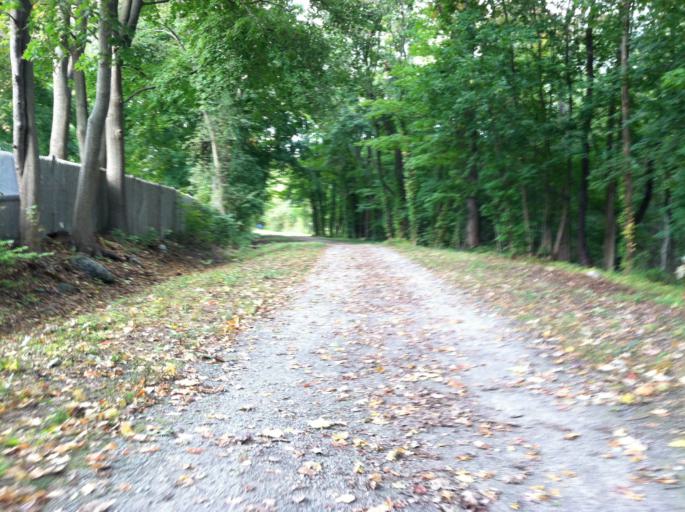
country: US
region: Massachusetts
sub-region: Middlesex County
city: Bedford
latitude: 42.4932
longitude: -71.2755
